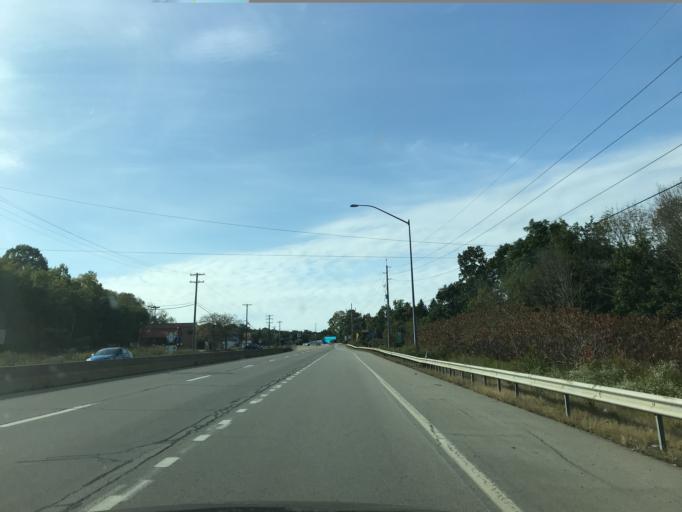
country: US
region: Pennsylvania
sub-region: Crawford County
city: Meadville
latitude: 41.6240
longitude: -80.1871
